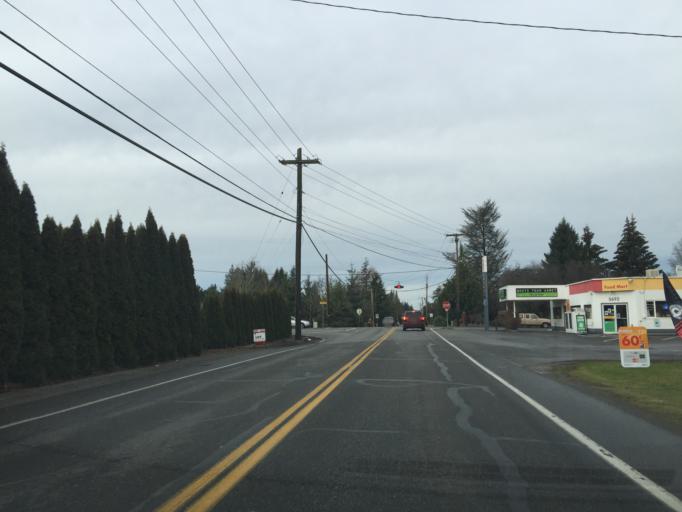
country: US
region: Washington
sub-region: Whatcom County
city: Ferndale
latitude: 48.8472
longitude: -122.5410
